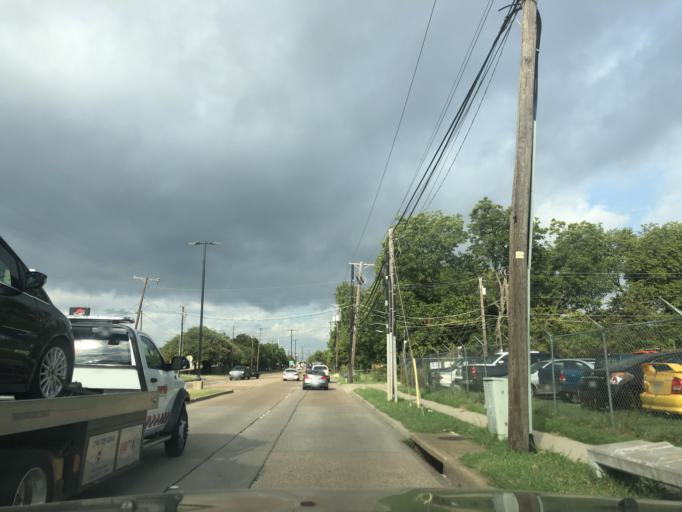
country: US
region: Texas
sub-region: Dallas County
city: Garland
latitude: 32.8790
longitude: -96.6605
